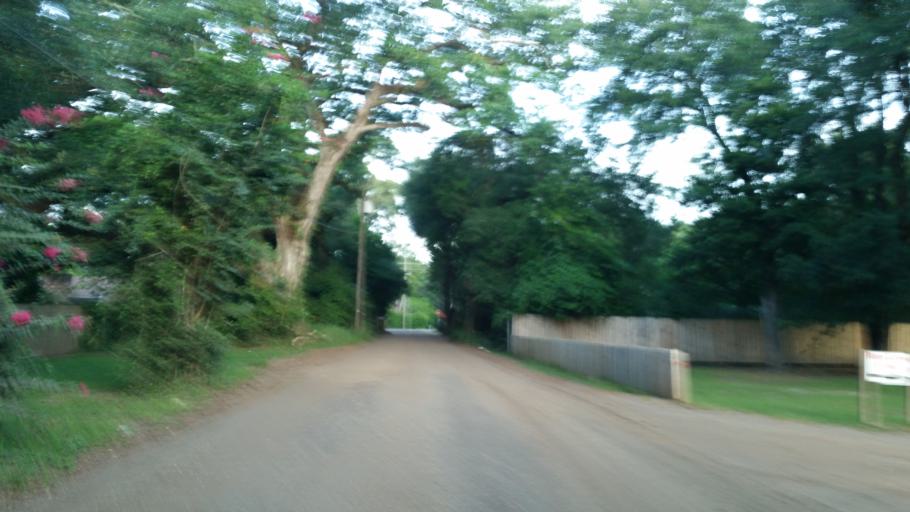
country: US
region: Florida
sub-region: Escambia County
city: Ensley
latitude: 30.5274
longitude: -87.3121
